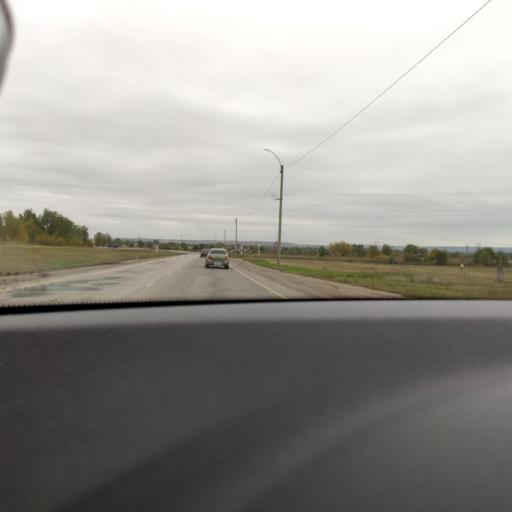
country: RU
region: Samara
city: Krasnyy Yar
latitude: 53.4771
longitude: 50.3916
